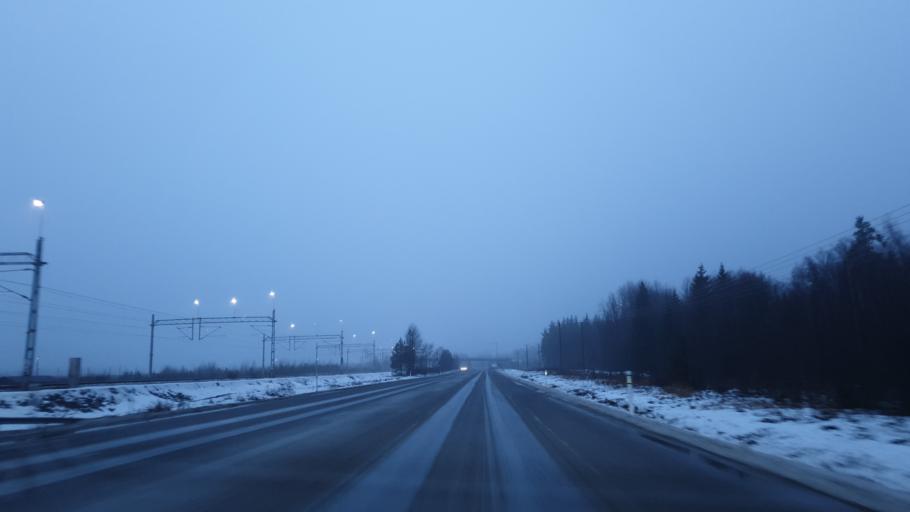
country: SE
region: Vaesterbotten
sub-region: Umea Kommun
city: Umea
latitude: 63.7855
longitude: 20.3184
